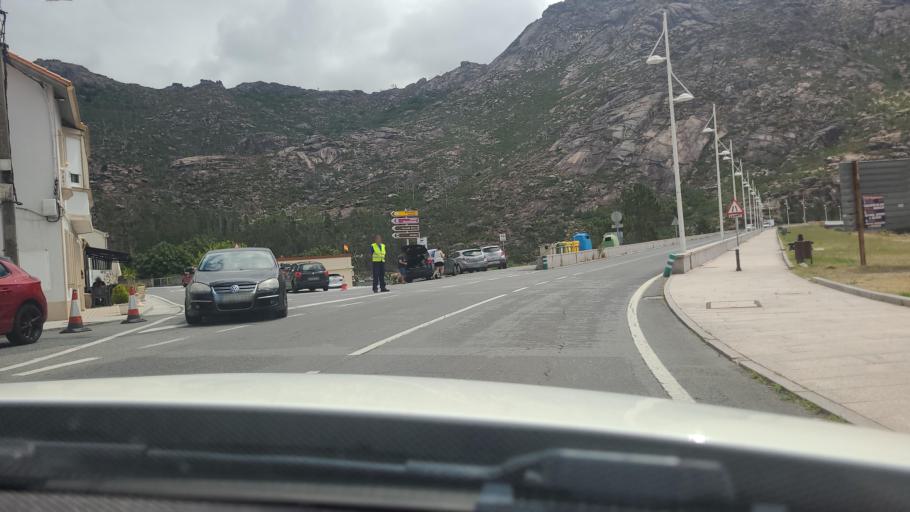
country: ES
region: Galicia
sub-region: Provincia da Coruna
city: Corcubion
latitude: 42.9080
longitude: -9.1270
